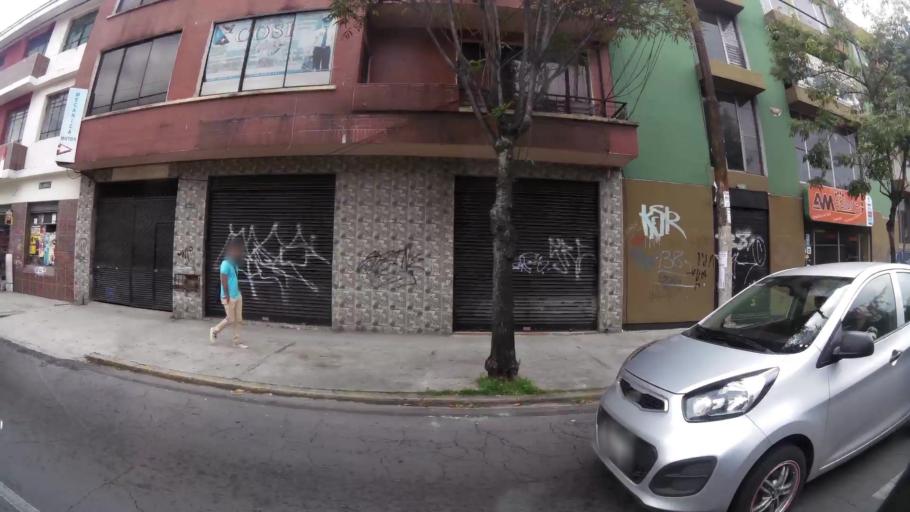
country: EC
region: Pichincha
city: Quito
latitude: -0.1952
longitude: -78.4992
